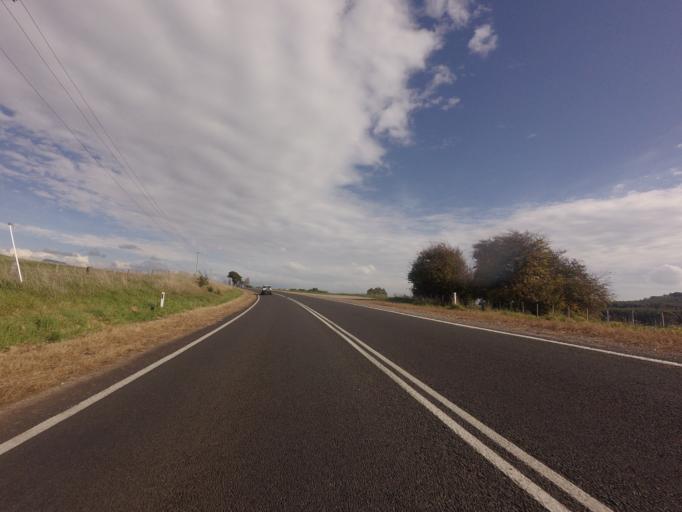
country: AU
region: Tasmania
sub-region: Meander Valley
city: Deloraine
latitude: -41.5185
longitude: 146.7228
